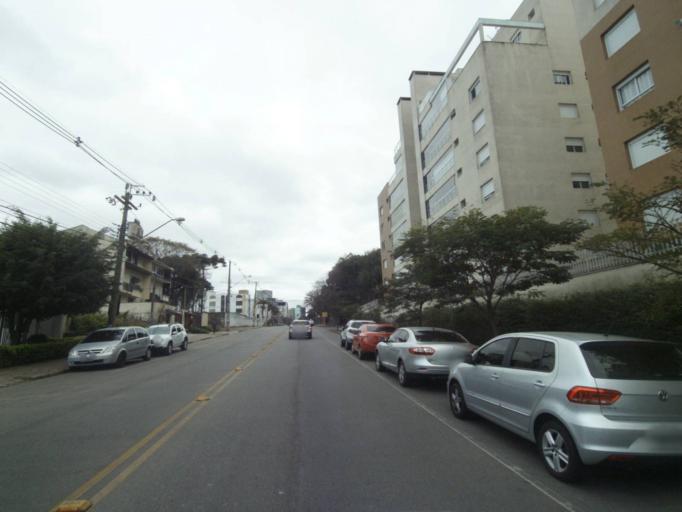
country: BR
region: Parana
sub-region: Curitiba
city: Curitiba
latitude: -25.4597
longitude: -49.2814
